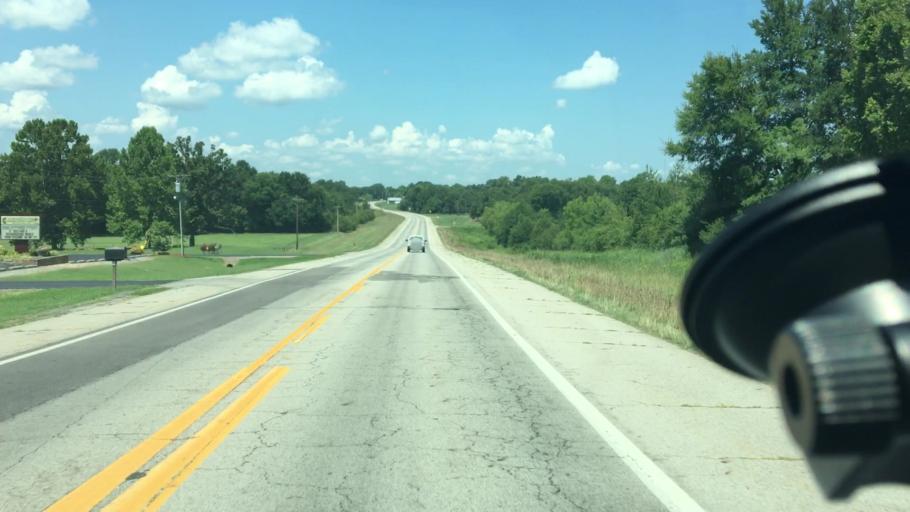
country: US
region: Arkansas
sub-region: Sebastian County
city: Lavaca
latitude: 35.2920
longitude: -94.1257
